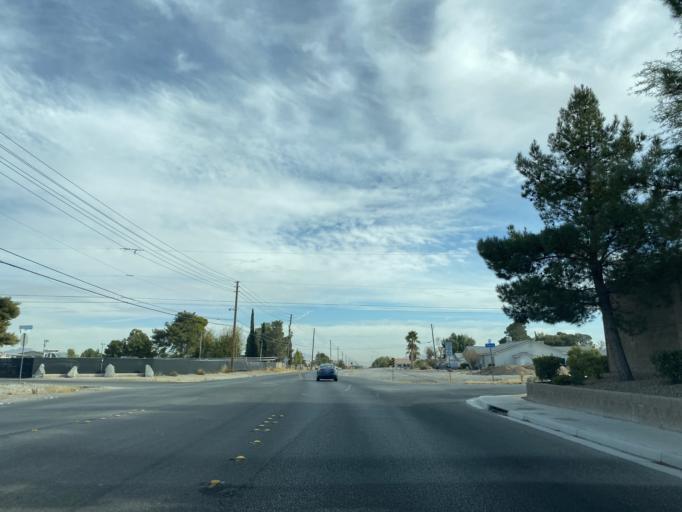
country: US
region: Nevada
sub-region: Clark County
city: North Las Vegas
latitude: 36.2468
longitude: -115.1876
